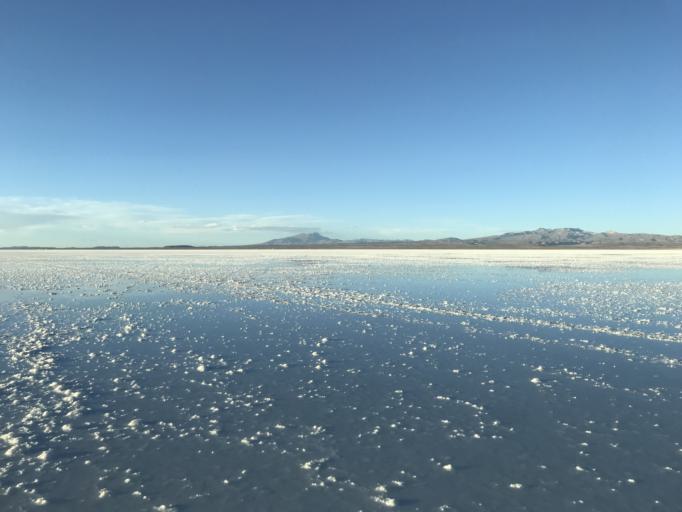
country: BO
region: Potosi
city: Colchani
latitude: -20.3833
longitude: -66.9865
